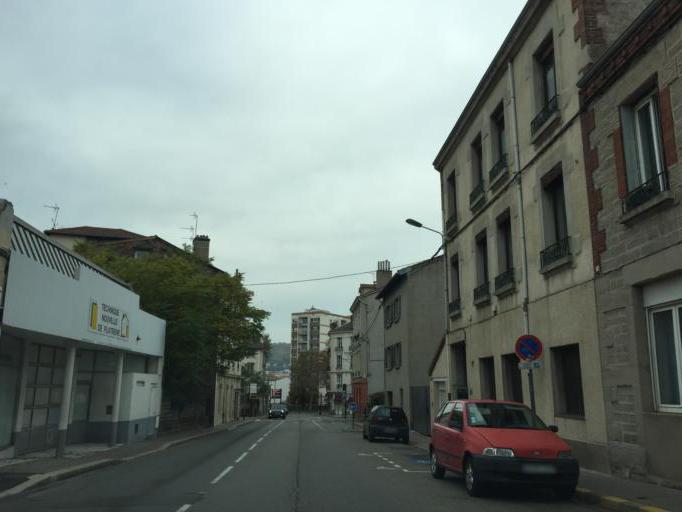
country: FR
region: Rhone-Alpes
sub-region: Departement de la Loire
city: Saint-Etienne
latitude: 45.4465
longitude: 4.3989
